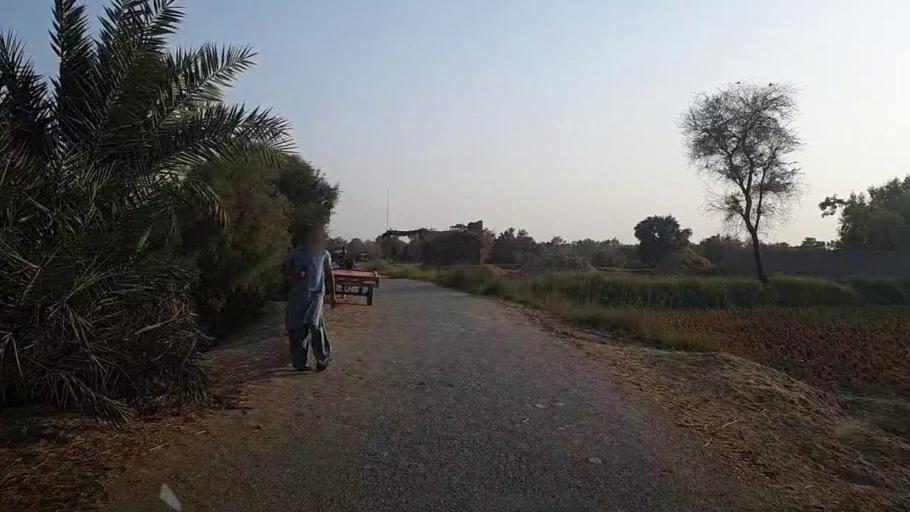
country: PK
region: Sindh
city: Kandhkot
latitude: 28.2403
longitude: 69.0931
